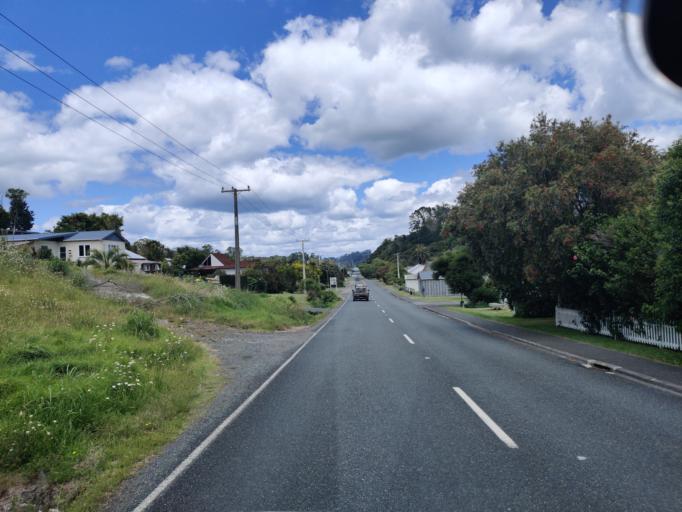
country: NZ
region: Northland
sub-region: Far North District
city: Paihia
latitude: -35.2645
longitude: 174.1241
